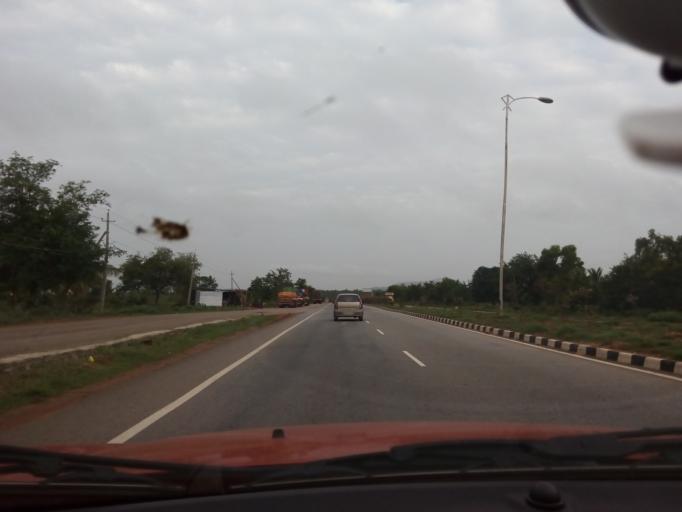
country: IN
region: Karnataka
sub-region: Mandya
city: Belluru
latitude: 12.9796
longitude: 76.8423
